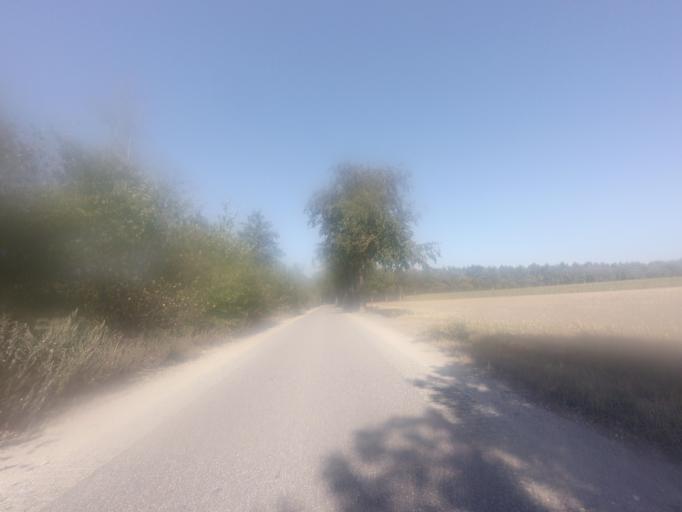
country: NL
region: North Brabant
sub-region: Gemeente Oirschot
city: Oostelbeers
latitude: 51.4875
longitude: 5.2660
